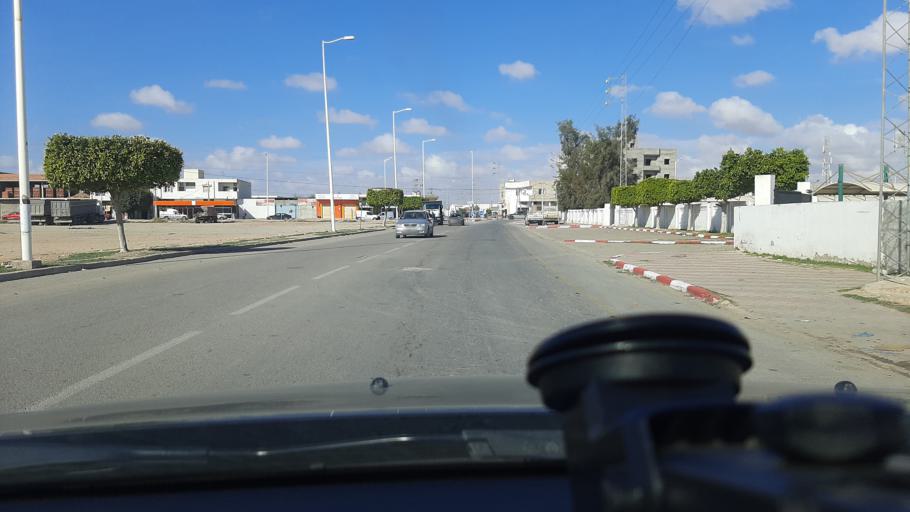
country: TN
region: Safaqis
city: Sfax
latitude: 34.8105
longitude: 10.7106
